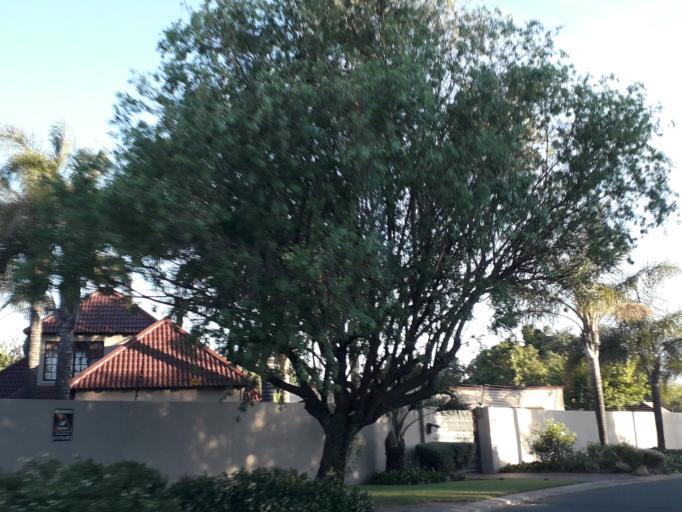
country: ZA
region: Gauteng
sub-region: City of Johannesburg Metropolitan Municipality
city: Roodepoort
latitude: -26.1589
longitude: 27.9525
